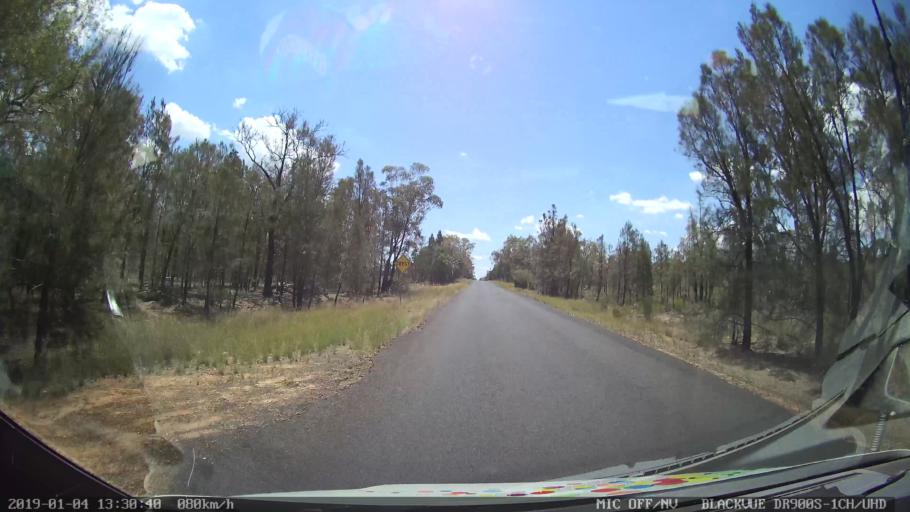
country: AU
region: New South Wales
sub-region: Parkes
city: Peak Hill
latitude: -32.6322
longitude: 148.5493
